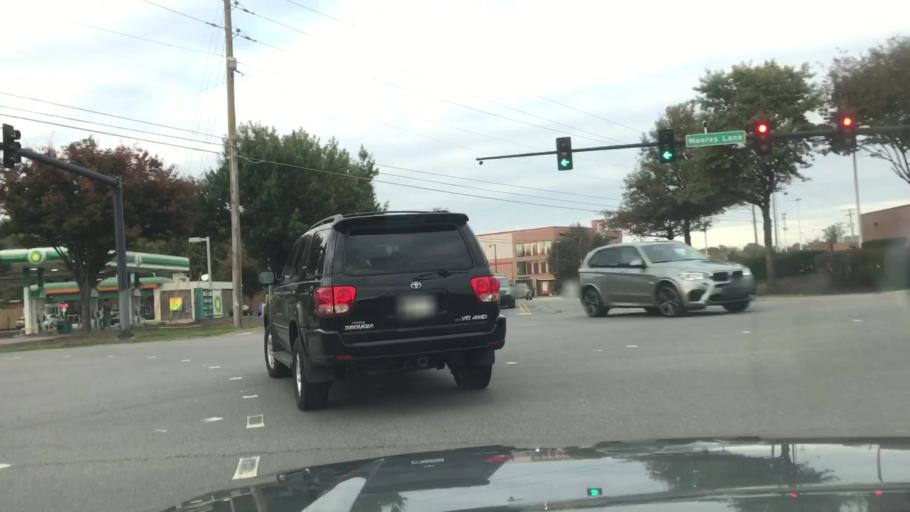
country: US
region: Tennessee
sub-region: Williamson County
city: Brentwood Estates
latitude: 35.9670
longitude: -86.8135
